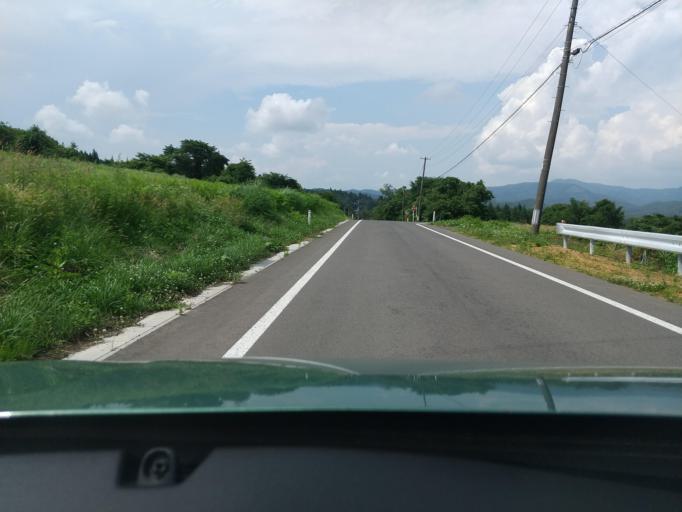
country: JP
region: Iwate
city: Ichinoseki
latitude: 39.0001
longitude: 141.2183
